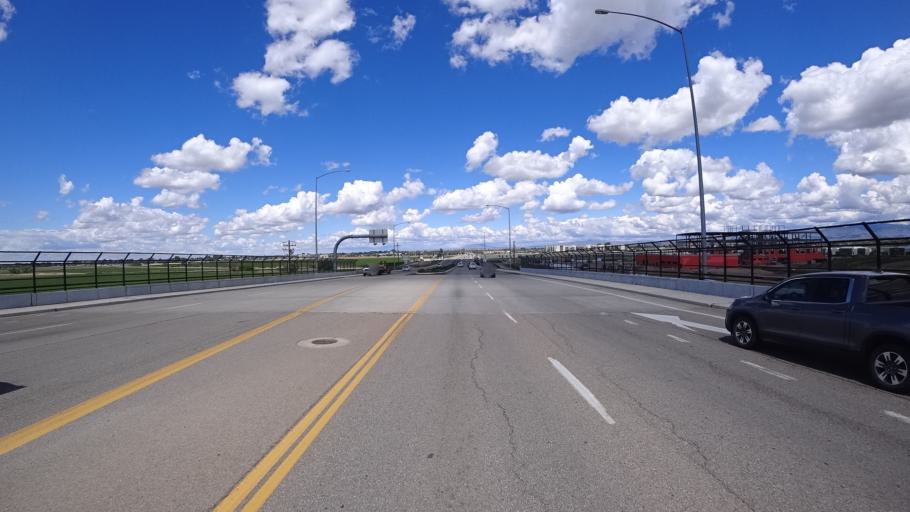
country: US
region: Idaho
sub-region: Ada County
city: Meridian
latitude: 43.5949
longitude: -116.4338
